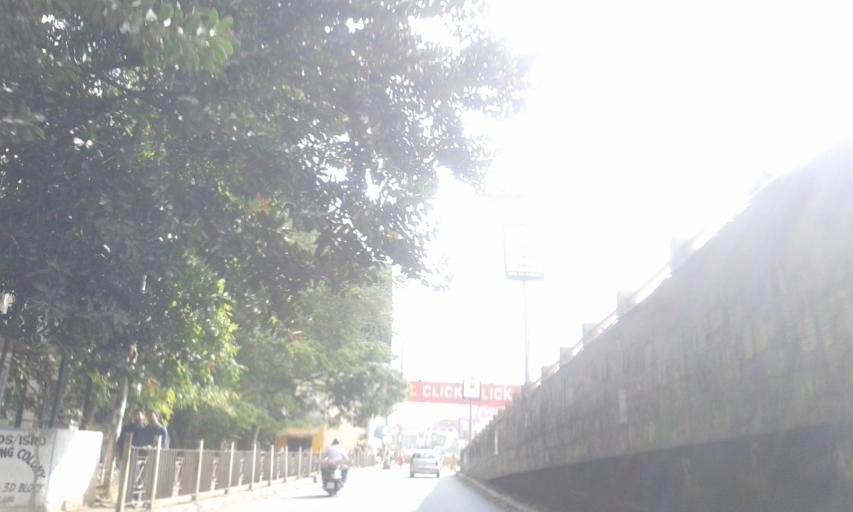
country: IN
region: Karnataka
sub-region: Bangalore Urban
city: Bangalore
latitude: 12.9592
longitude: 77.6416
